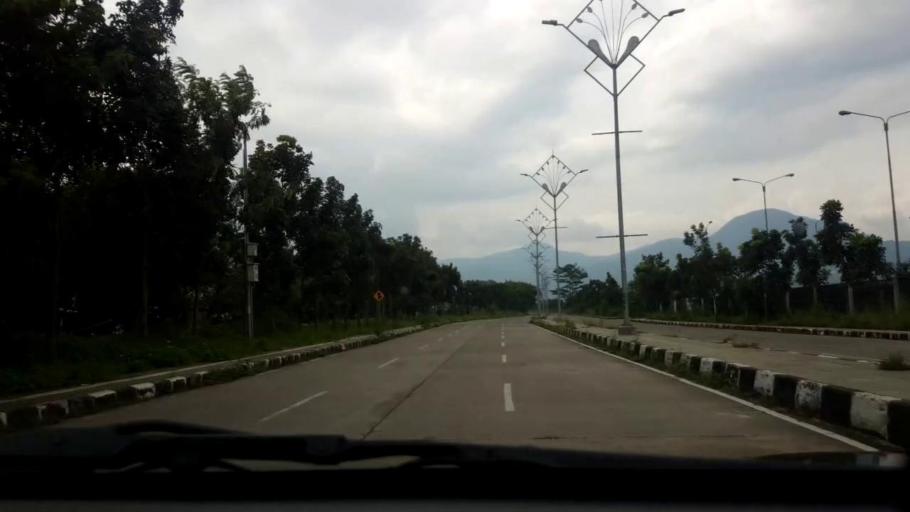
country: ID
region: West Java
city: Cileunyi
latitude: -6.9552
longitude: 107.7107
